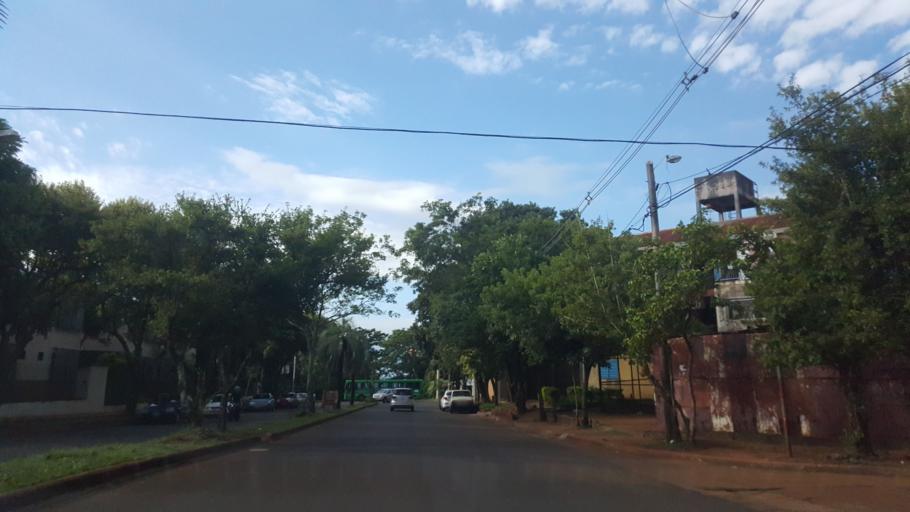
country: AR
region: Misiones
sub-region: Departamento de Capital
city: Posadas
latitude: -27.3582
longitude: -55.9304
